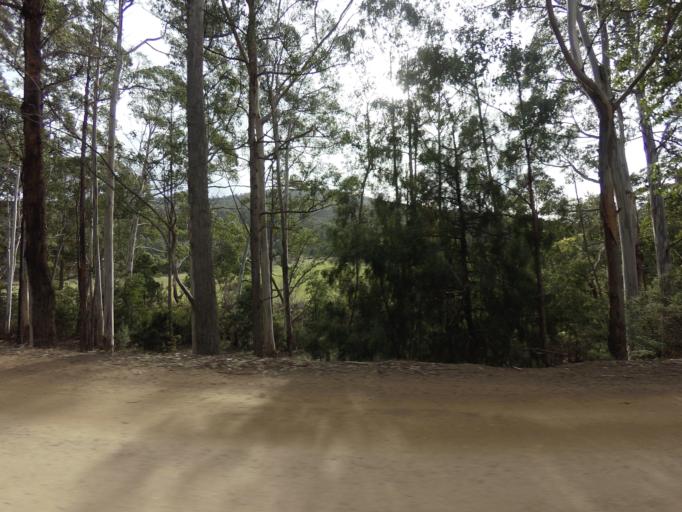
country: AU
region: Tasmania
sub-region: Huon Valley
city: Huonville
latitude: -43.0735
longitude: 147.0783
